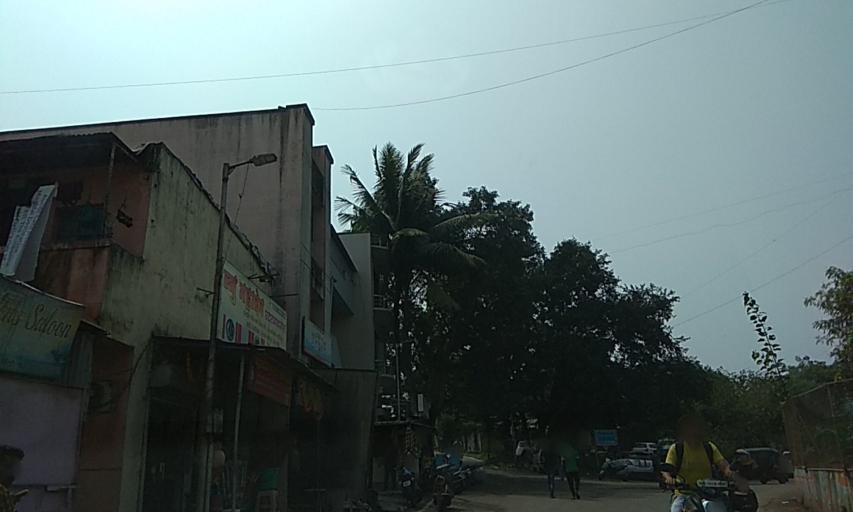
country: IN
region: Maharashtra
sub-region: Pune Division
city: Pimpri
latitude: 18.5606
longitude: 73.7864
